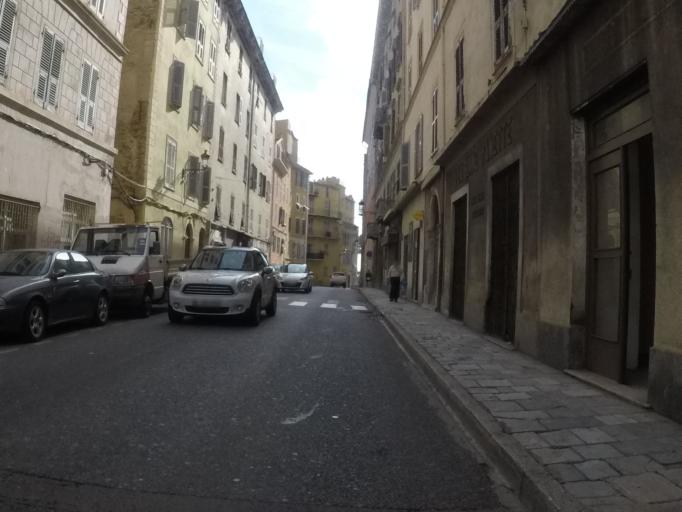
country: FR
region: Corsica
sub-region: Departement de la Haute-Corse
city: Bastia
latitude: 42.6951
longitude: 9.4483
